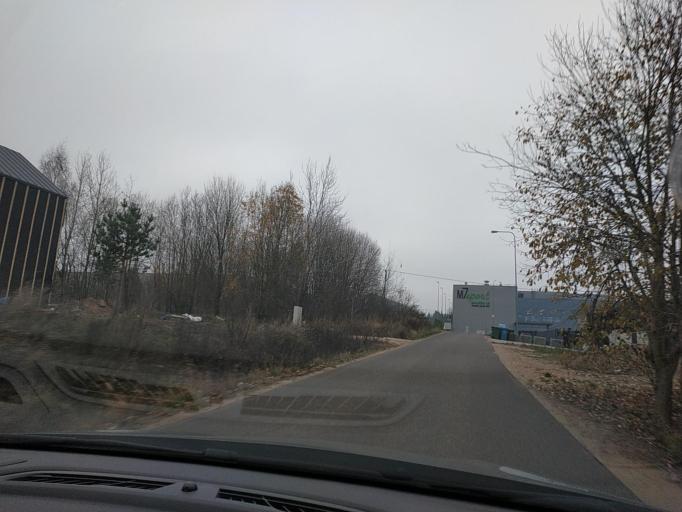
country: LT
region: Vilnius County
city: Rasos
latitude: 54.6404
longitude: 25.3342
